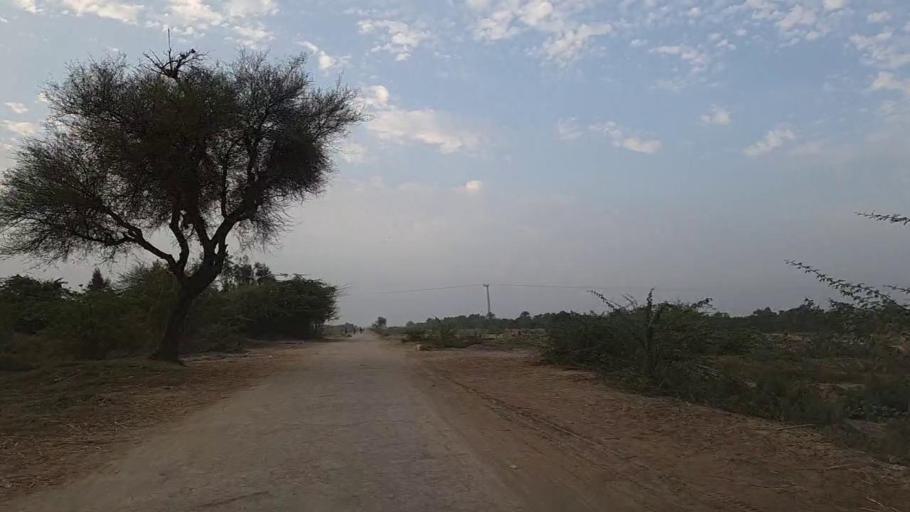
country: PK
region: Sindh
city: Mirwah Gorchani
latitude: 25.3189
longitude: 69.2207
